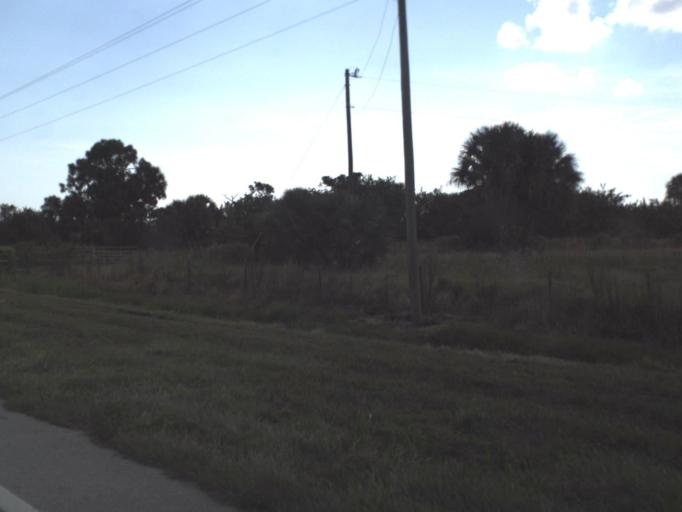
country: US
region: Florida
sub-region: Okeechobee County
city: Okeechobee
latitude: 27.2930
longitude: -80.8887
